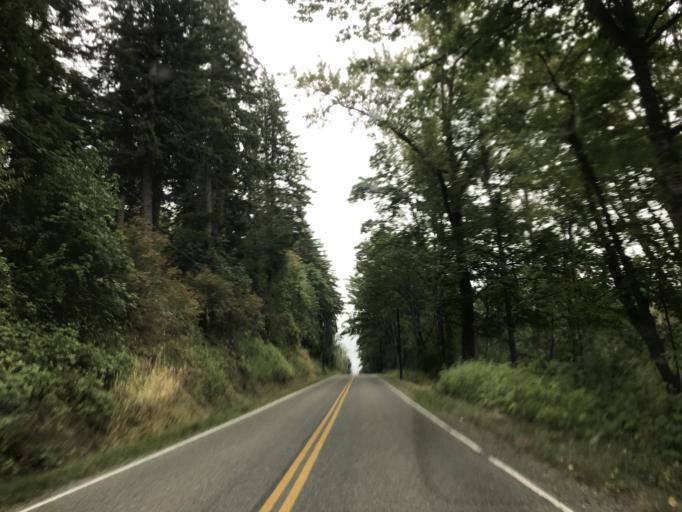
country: US
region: Washington
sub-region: Whatcom County
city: Sudden Valley
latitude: 48.7833
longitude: -122.3331
